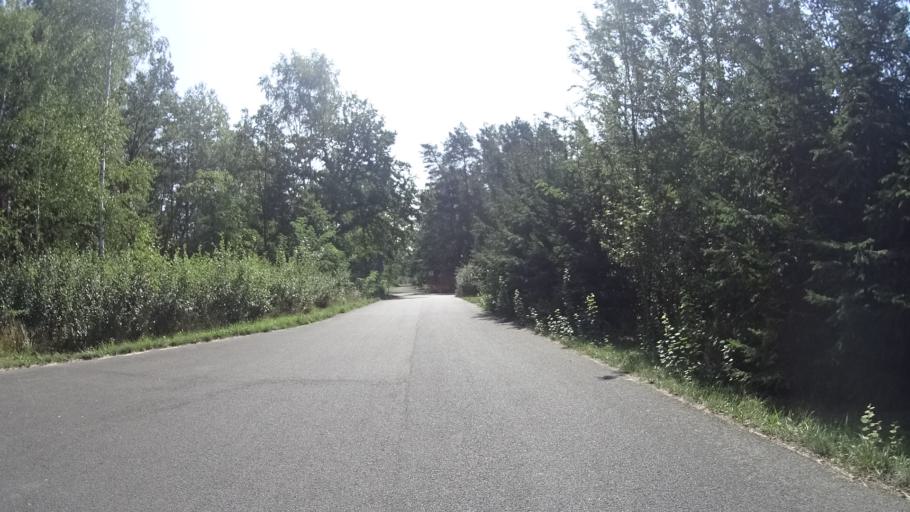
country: DE
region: Brandenburg
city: Cottbus
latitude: 51.7974
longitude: 14.2946
